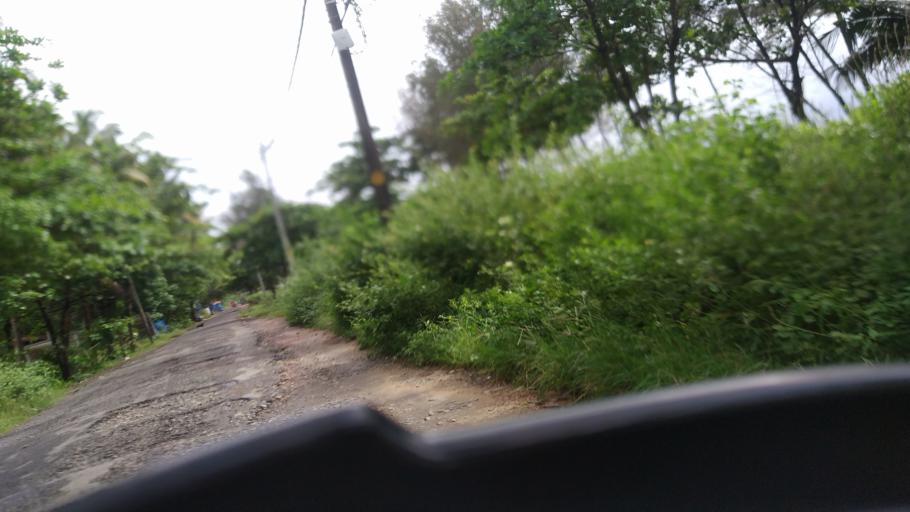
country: IN
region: Kerala
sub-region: Thrissur District
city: Kodungallur
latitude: 10.1288
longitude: 76.1826
